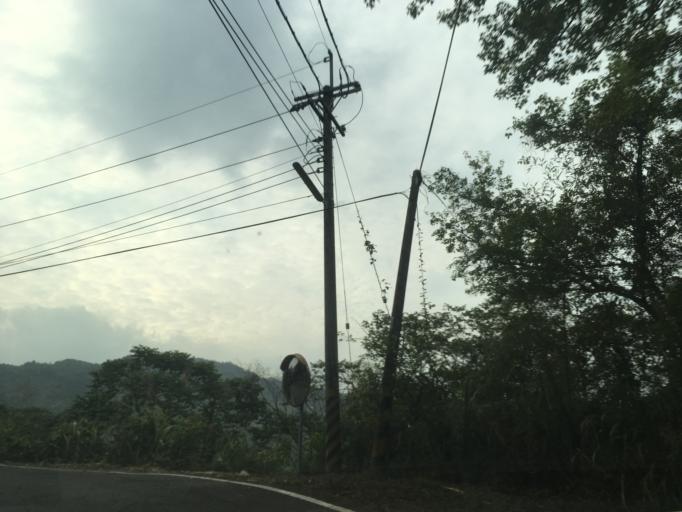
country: TW
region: Taiwan
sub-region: Nantou
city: Puli
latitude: 23.9476
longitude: 120.8535
